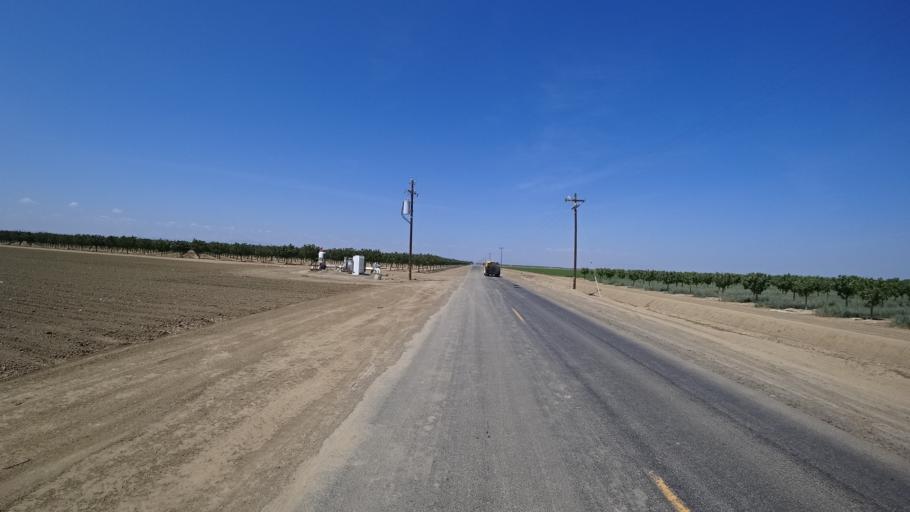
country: US
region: California
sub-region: Kings County
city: Kettleman City
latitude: 36.1377
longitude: -119.9585
